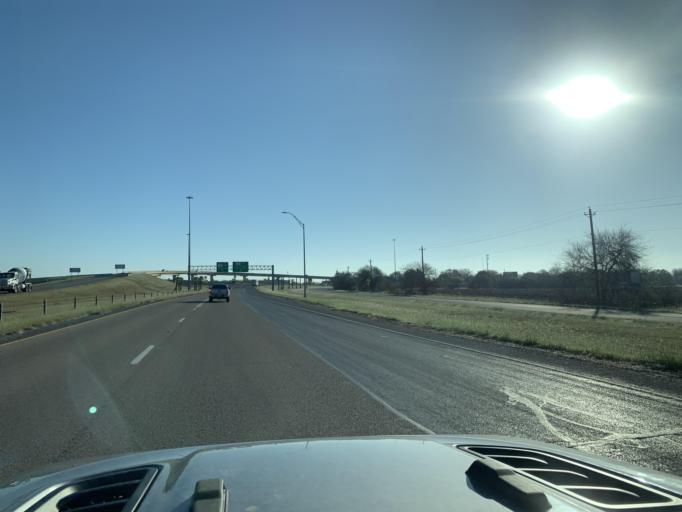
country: US
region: Texas
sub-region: Nueces County
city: Corpus Christi
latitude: 27.7817
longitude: -97.4742
